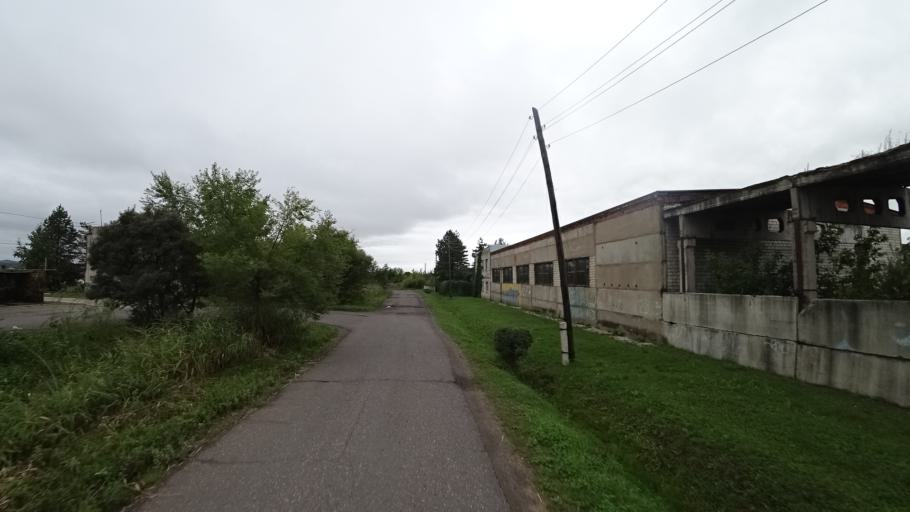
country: RU
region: Primorskiy
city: Chernigovka
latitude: 44.3299
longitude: 132.5279
